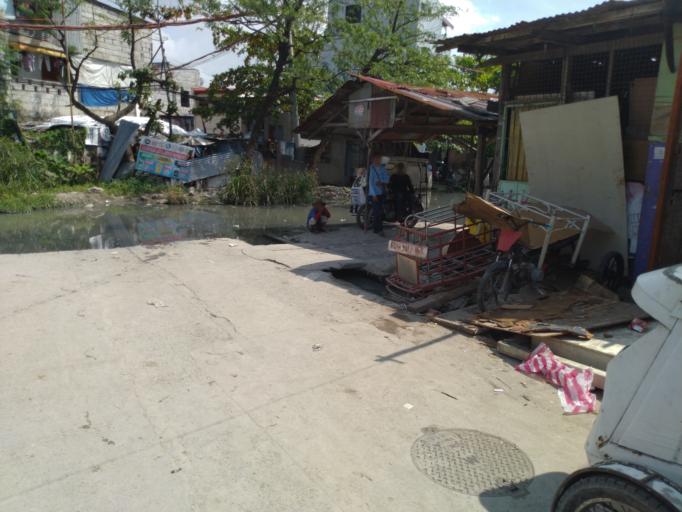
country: PH
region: Calabarzon
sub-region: Province of Rizal
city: Taytay
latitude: 14.5410
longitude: 121.1113
